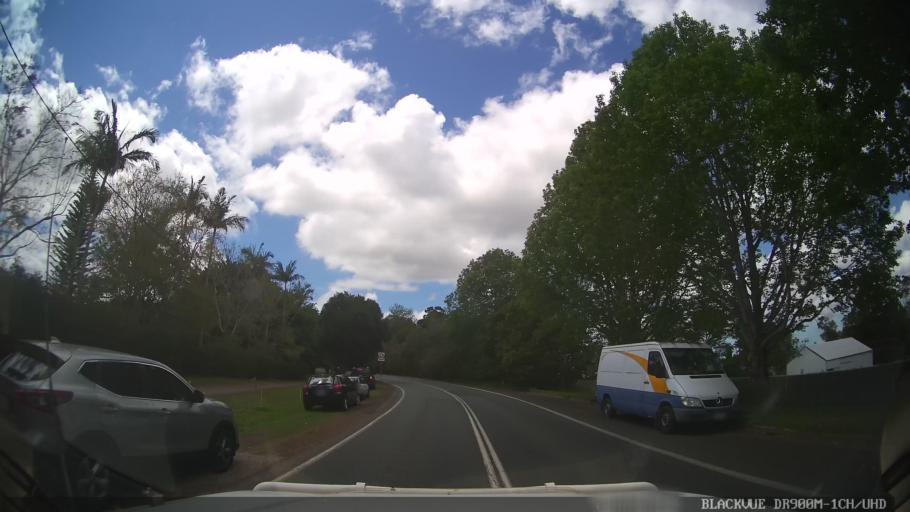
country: AU
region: Queensland
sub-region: Sunshine Coast
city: Nambour
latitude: -26.6629
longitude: 152.8809
